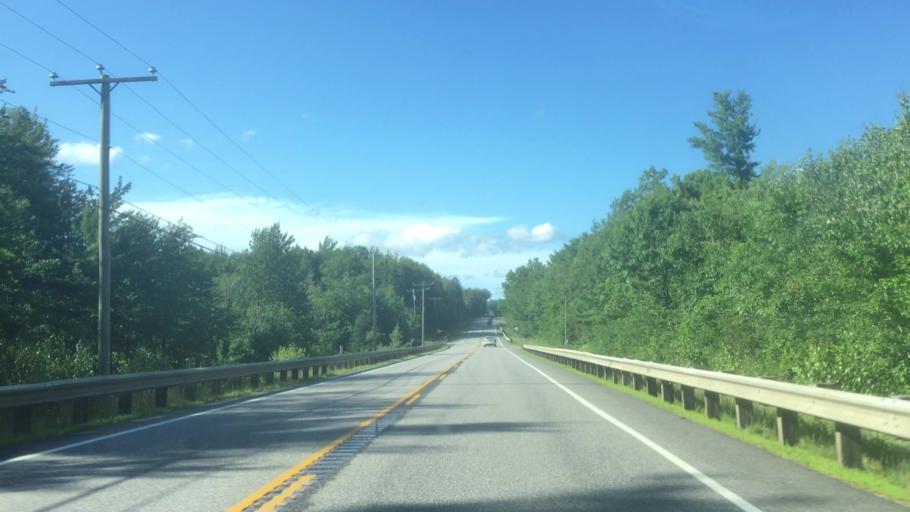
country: US
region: New Hampshire
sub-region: Cheshire County
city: Harrisville
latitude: 43.0493
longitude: -72.0775
